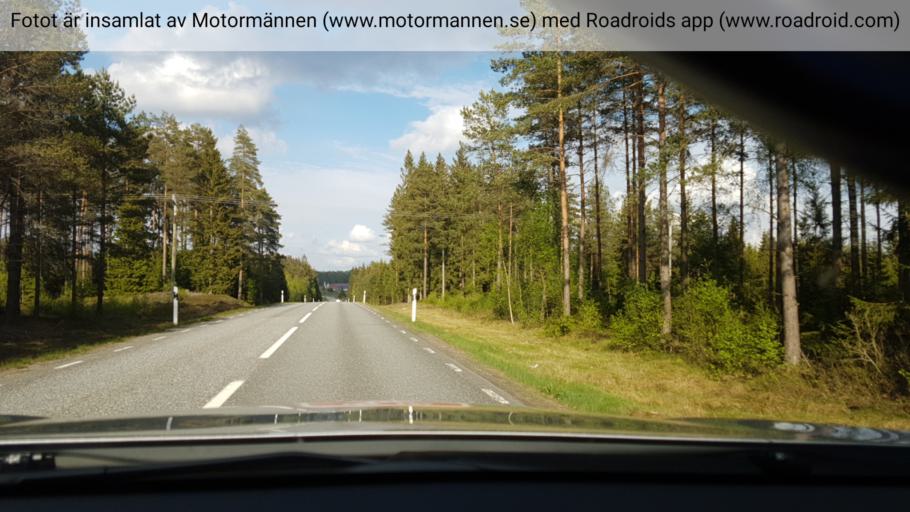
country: SE
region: Joenkoeping
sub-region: Vaggeryds Kommun
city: Skillingaryd
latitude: 57.3980
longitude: 14.0380
